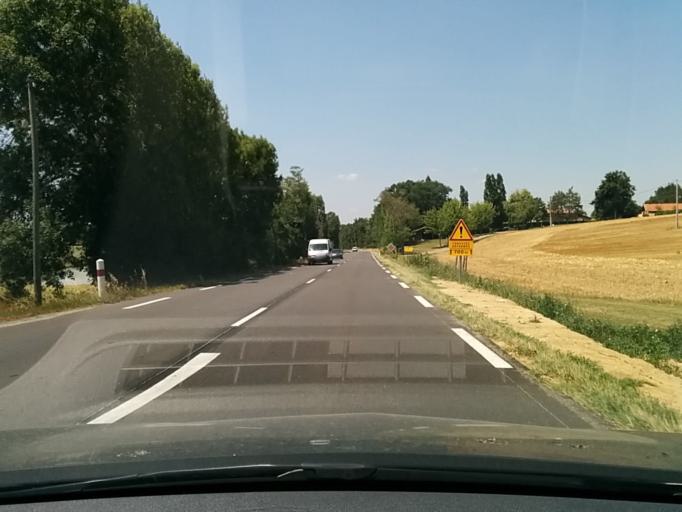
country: FR
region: Midi-Pyrenees
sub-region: Departement du Gers
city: Gimont
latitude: 43.6164
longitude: 0.9312
